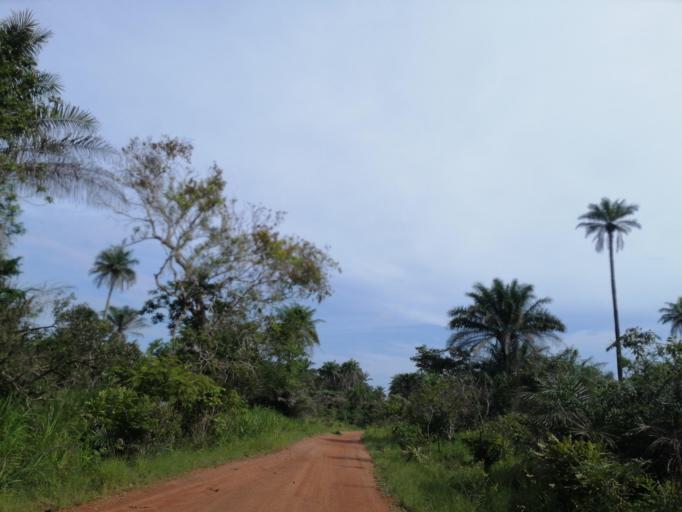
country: SL
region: Northern Province
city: Port Loko
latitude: 8.7812
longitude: -12.9216
